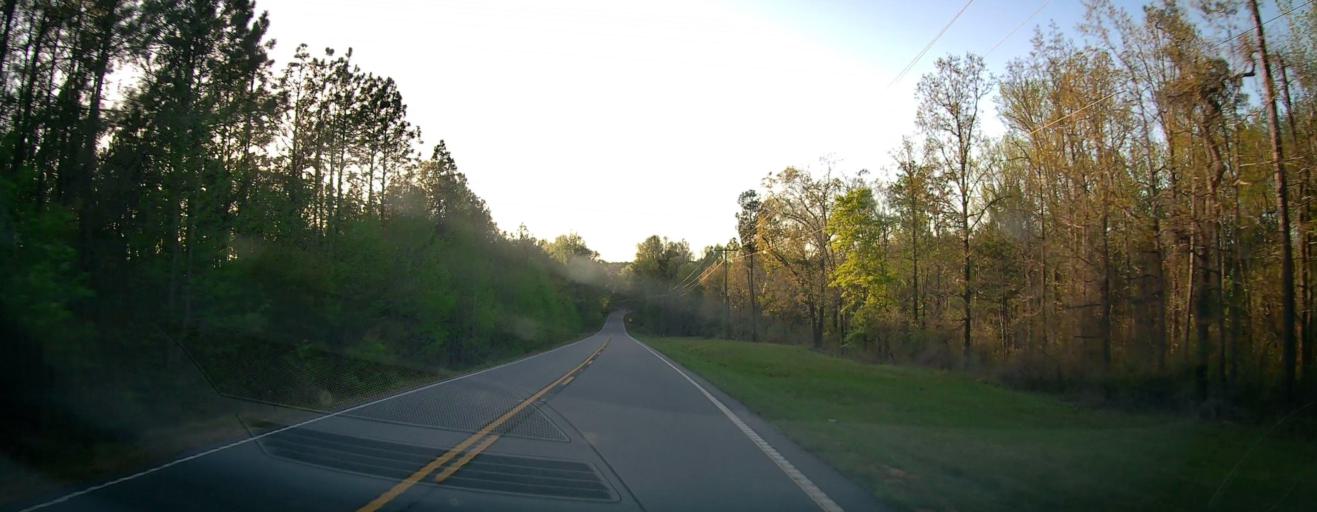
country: US
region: Georgia
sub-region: Talbot County
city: Talbotton
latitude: 32.5566
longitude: -84.5378
